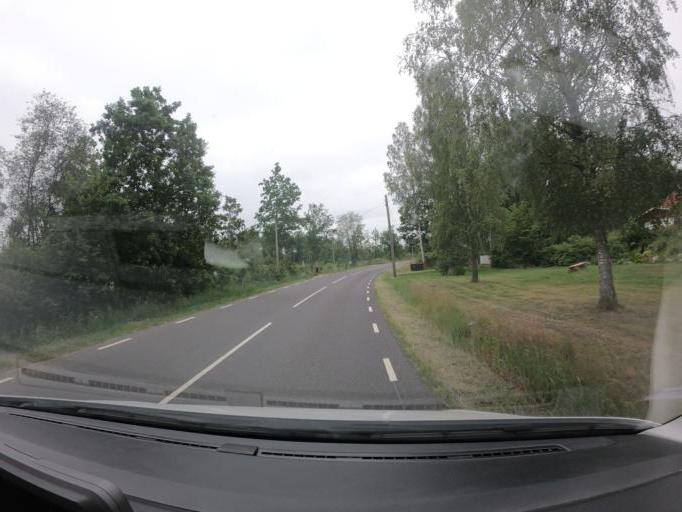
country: SE
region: Skane
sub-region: Perstorps Kommun
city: Perstorp
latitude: 56.0375
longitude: 13.3640
